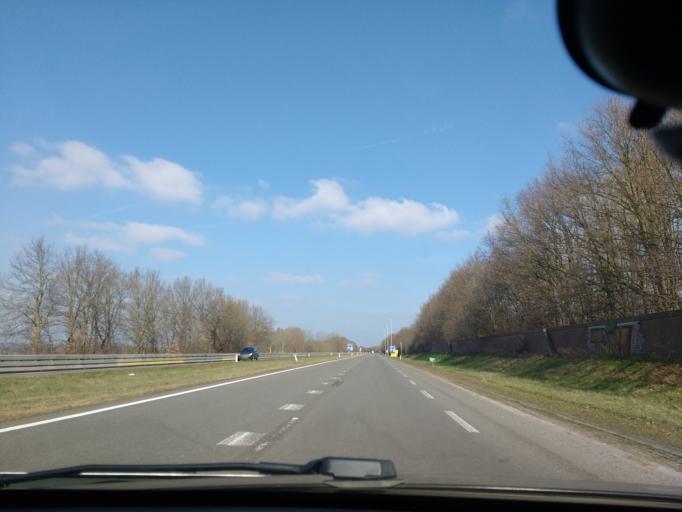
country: NL
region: Limburg
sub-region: Gemeente Gennep
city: Gennep
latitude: 51.6990
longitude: 5.9638
